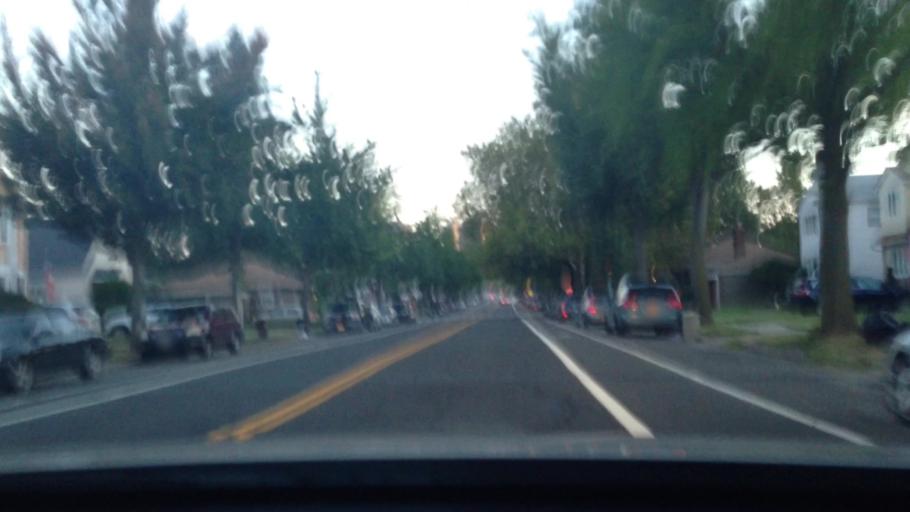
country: US
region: New York
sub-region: Nassau County
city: North New Hyde Park
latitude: 40.7446
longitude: -73.7080
